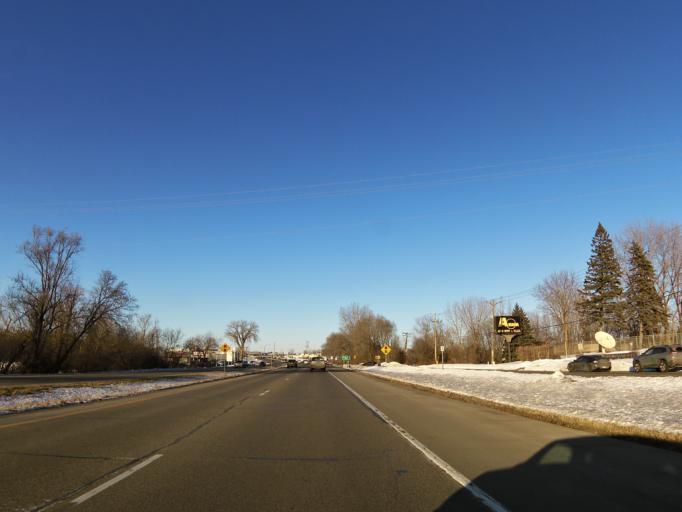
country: US
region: Minnesota
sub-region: Ramsey County
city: Little Canada
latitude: 45.0251
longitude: -93.0481
